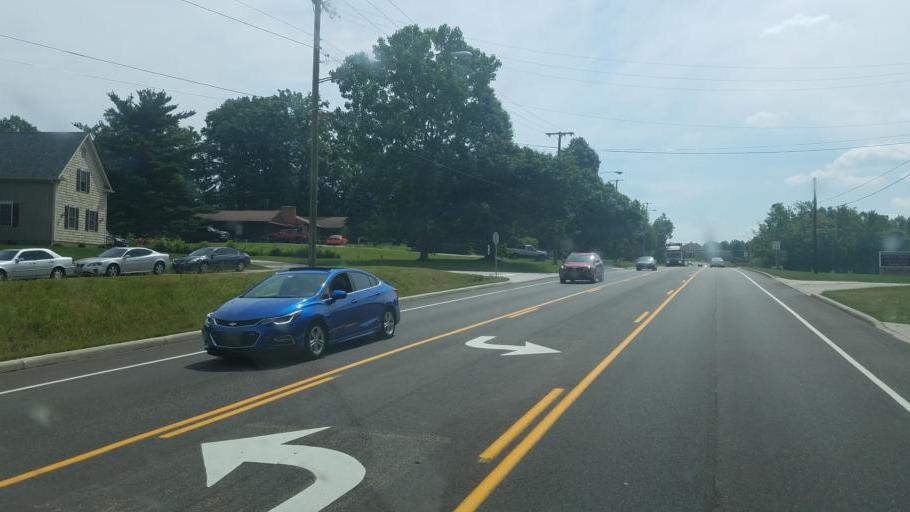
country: US
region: Ohio
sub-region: Summit County
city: Macedonia
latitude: 41.3129
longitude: -81.4942
